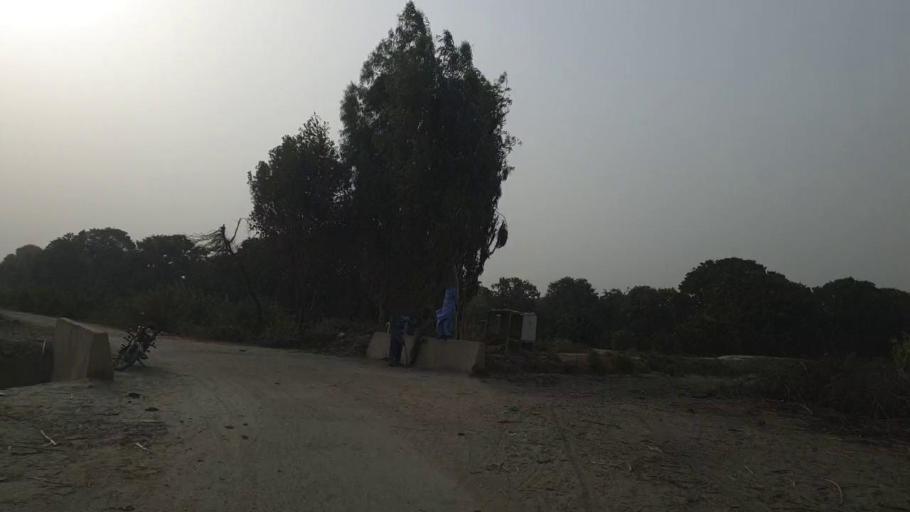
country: PK
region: Sindh
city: Kunri
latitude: 25.0669
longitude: 69.4449
